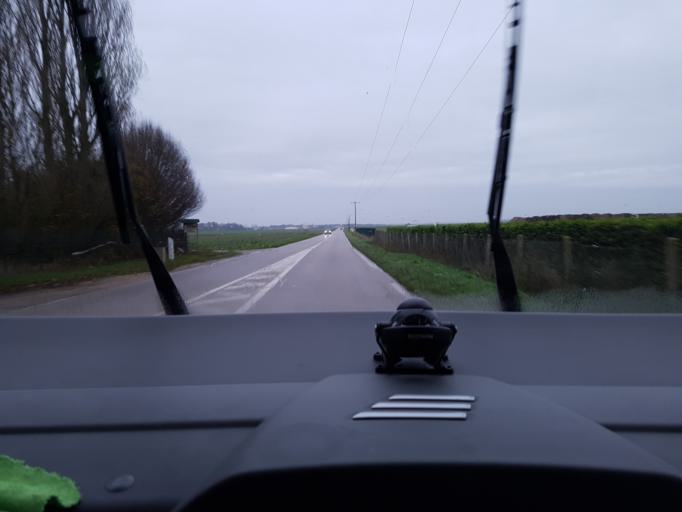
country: FR
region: Haute-Normandie
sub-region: Departement de l'Eure
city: Le Neubourg
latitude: 49.1473
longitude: 0.9402
